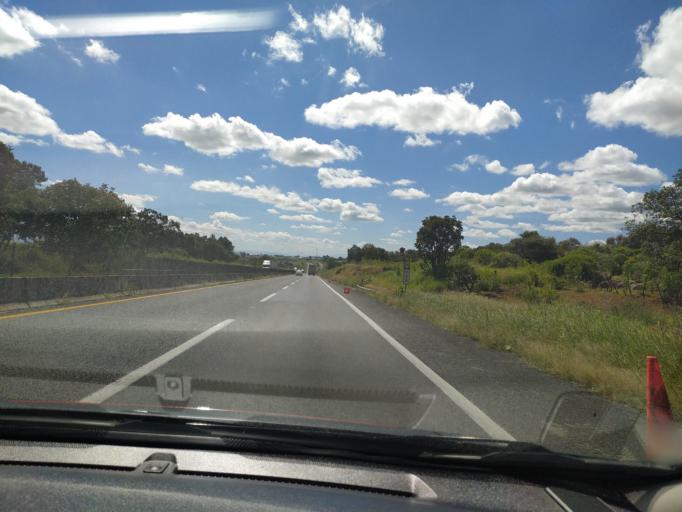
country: MX
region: Jalisco
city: Tepatitlan de Morelos
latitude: 20.8554
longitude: -102.7713
